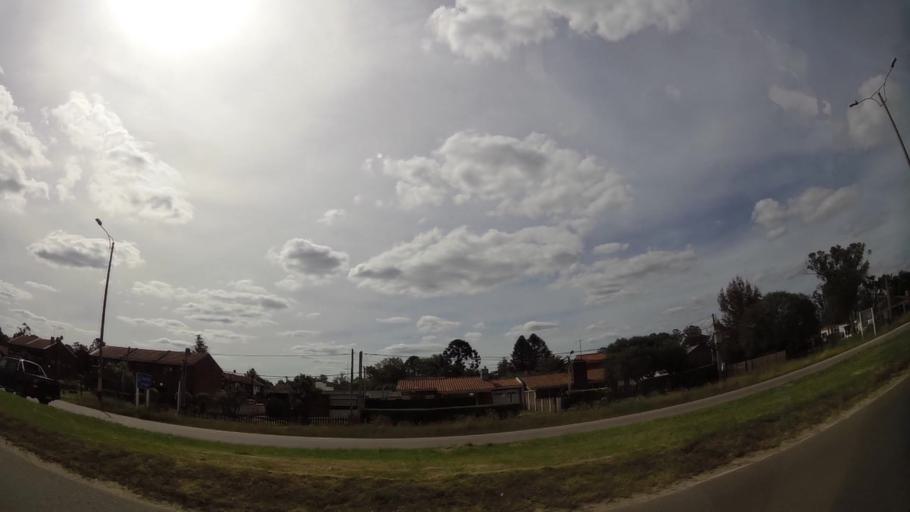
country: UY
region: Canelones
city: Colonia Nicolich
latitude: -34.8213
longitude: -55.9570
